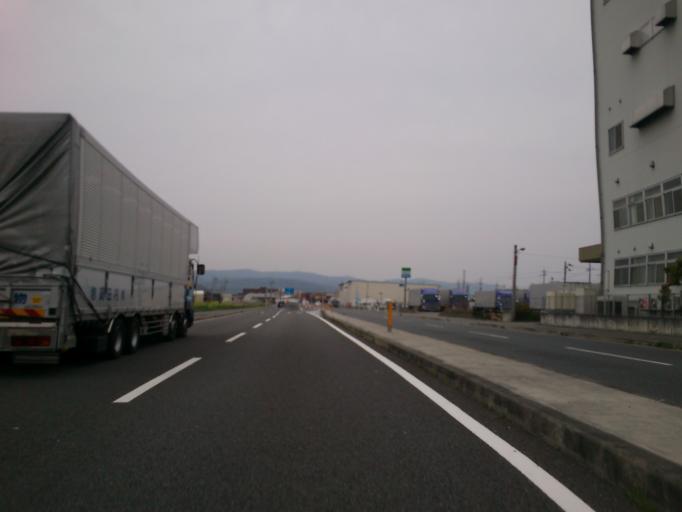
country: JP
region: Kyoto
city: Yawata
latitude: 34.8655
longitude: 135.7327
